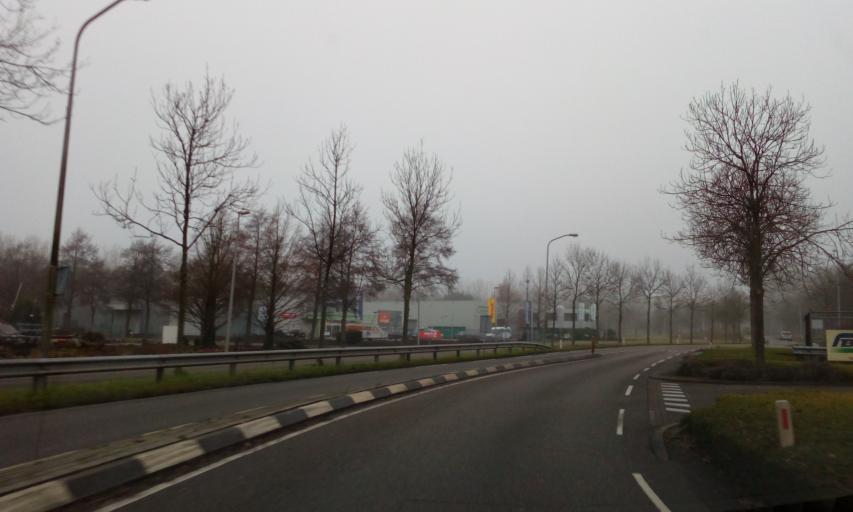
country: NL
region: South Holland
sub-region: Gemeente Capelle aan den IJssel
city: Capelle aan den IJssel
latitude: 51.9678
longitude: 4.5994
